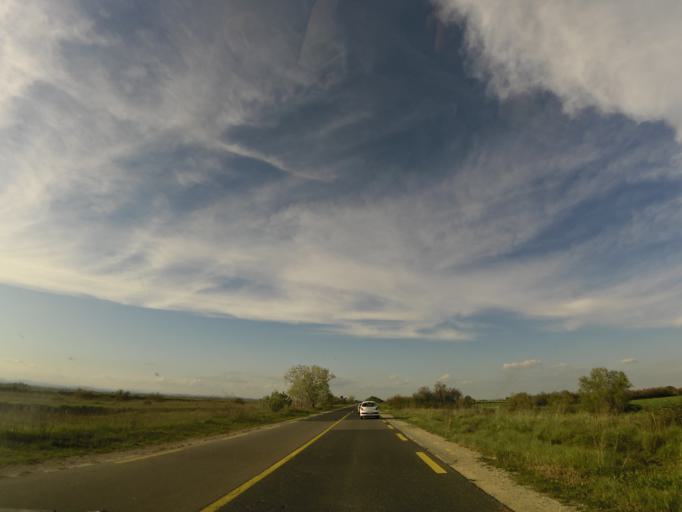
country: FR
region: Languedoc-Roussillon
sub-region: Departement de l'Herault
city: La Grande-Motte
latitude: 43.5908
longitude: 4.1047
